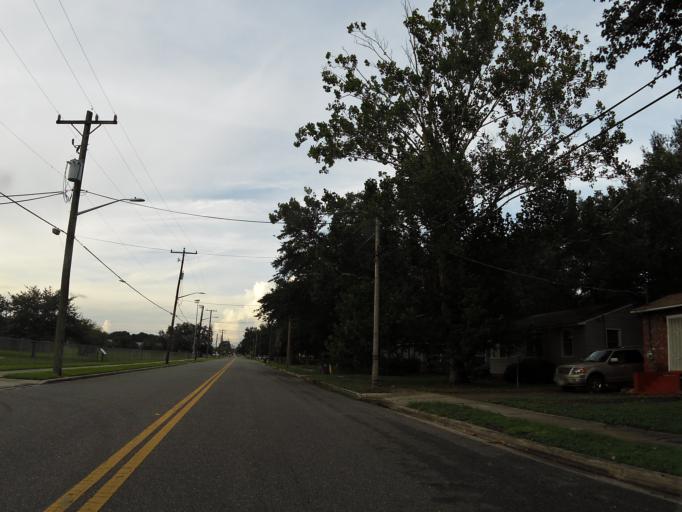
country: US
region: Florida
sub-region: Duval County
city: Jacksonville
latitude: 30.3482
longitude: -81.7228
